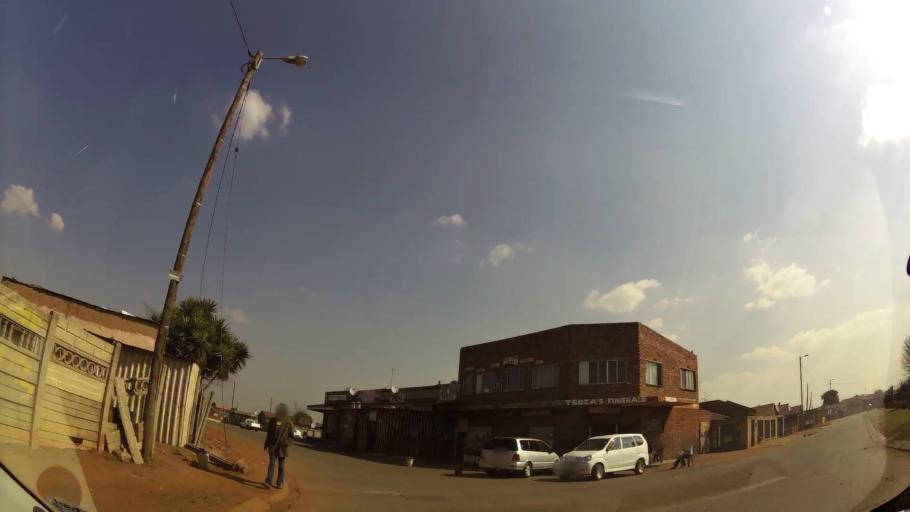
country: ZA
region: Gauteng
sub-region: Ekurhuleni Metropolitan Municipality
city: Brakpan
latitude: -26.1515
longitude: 28.4100
